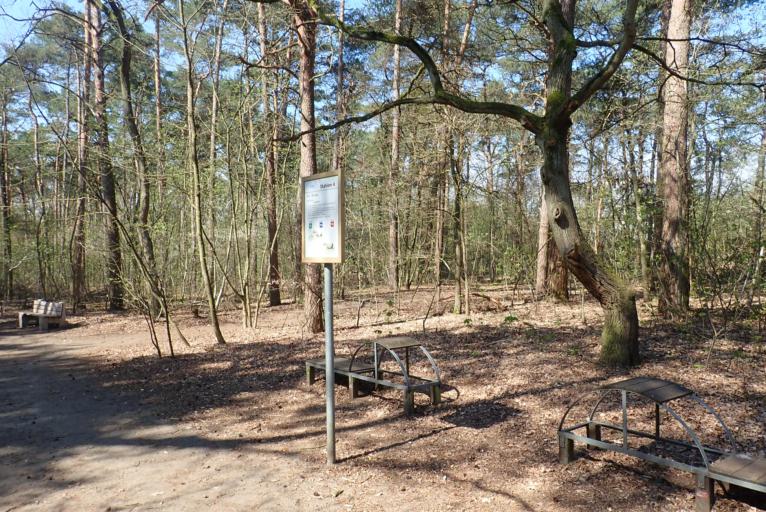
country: BE
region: Flanders
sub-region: Provincie Antwerpen
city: Brasschaat
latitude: 51.2985
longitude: 4.4630
